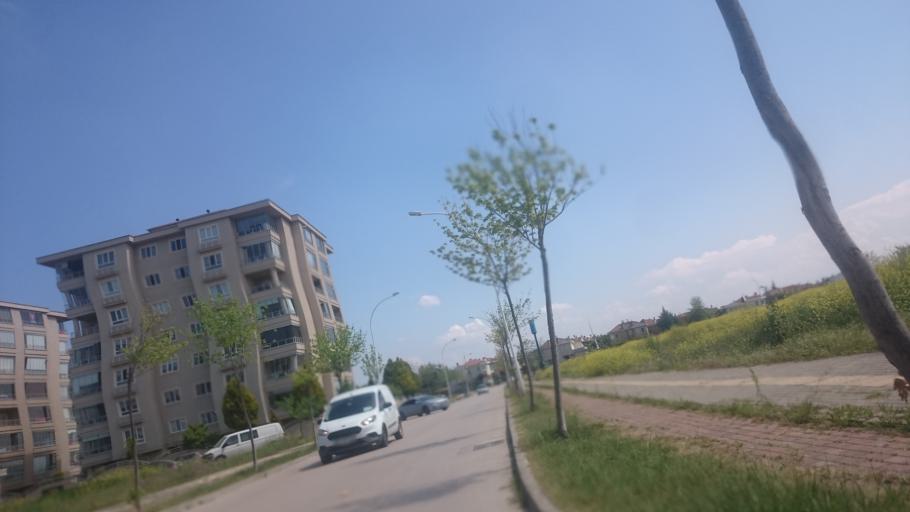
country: TR
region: Bursa
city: Cali
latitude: 40.2291
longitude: 28.9195
